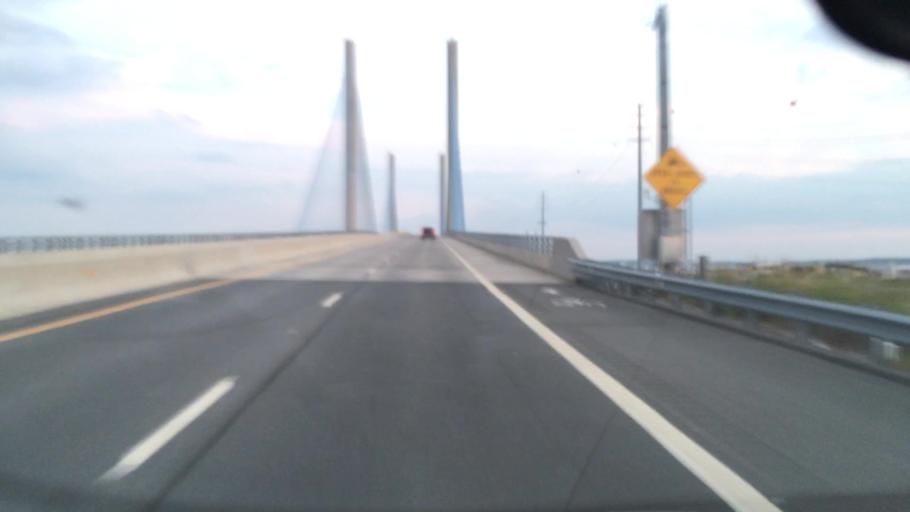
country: US
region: Delaware
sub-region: Sussex County
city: Ocean View
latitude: 38.6118
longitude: -75.0644
